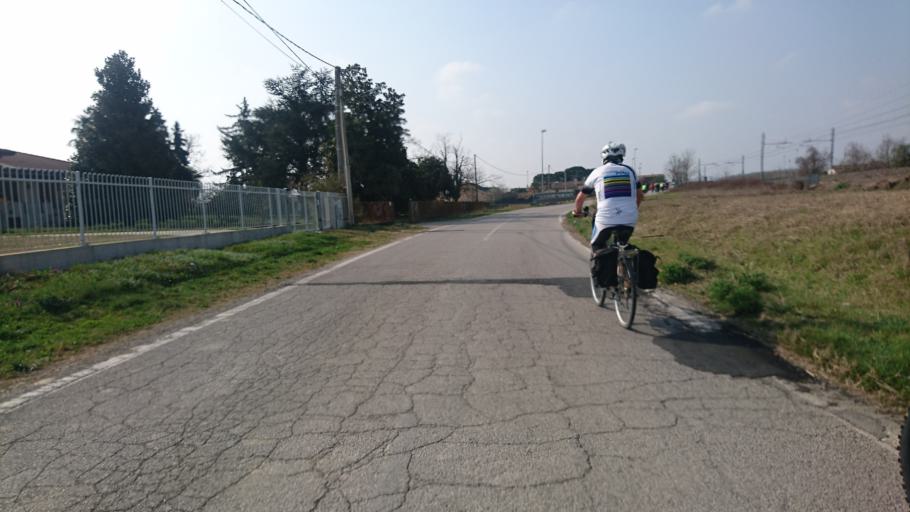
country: IT
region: Veneto
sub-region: Provincia di Padova
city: Mandriola-Sant'Agostino
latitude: 45.3767
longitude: 11.8282
